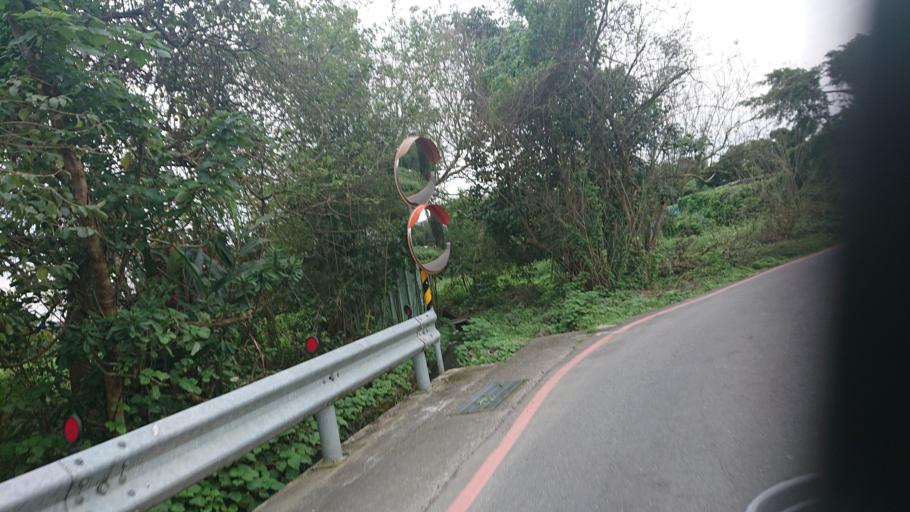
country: TW
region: Taiwan
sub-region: Taoyuan
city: Taoyuan
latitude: 24.9495
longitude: 121.3725
